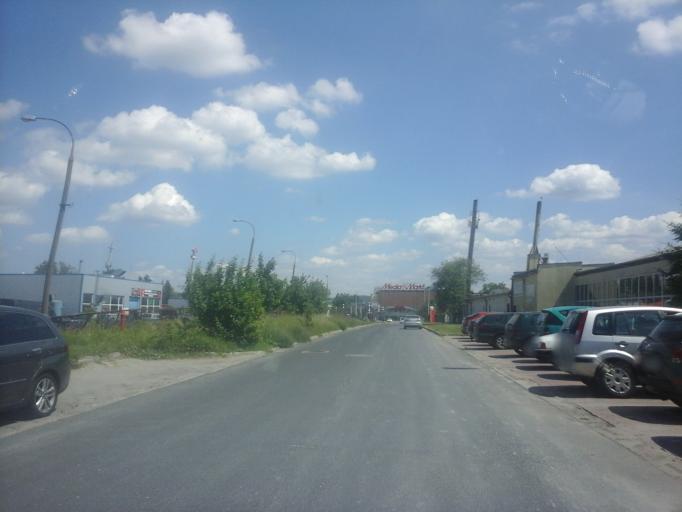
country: PL
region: West Pomeranian Voivodeship
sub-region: Koszalin
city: Koszalin
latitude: 54.1756
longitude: 16.1952
